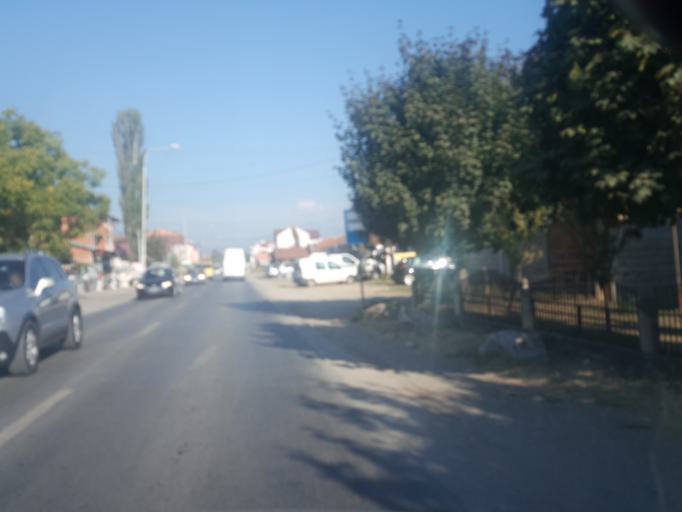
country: XK
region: Gjakova
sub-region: Komuna e Gjakoves
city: Gjakove
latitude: 42.4014
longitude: 20.4145
